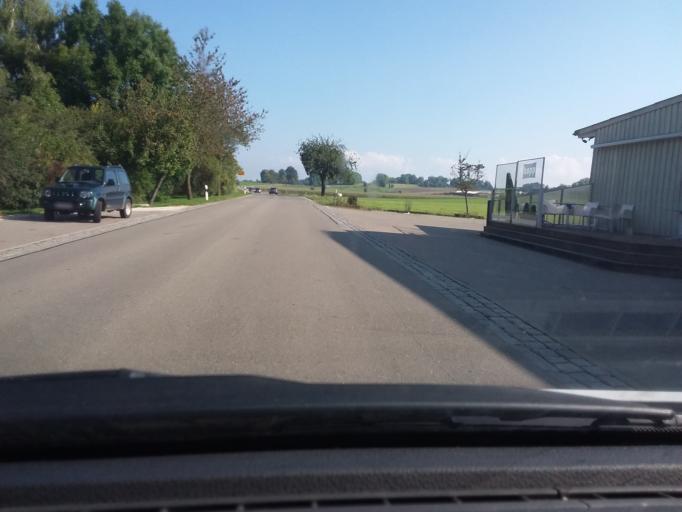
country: DE
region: Baden-Wuerttemberg
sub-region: Regierungsbezirk Stuttgart
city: Bad Uberkingen
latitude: 48.5887
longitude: 9.8073
